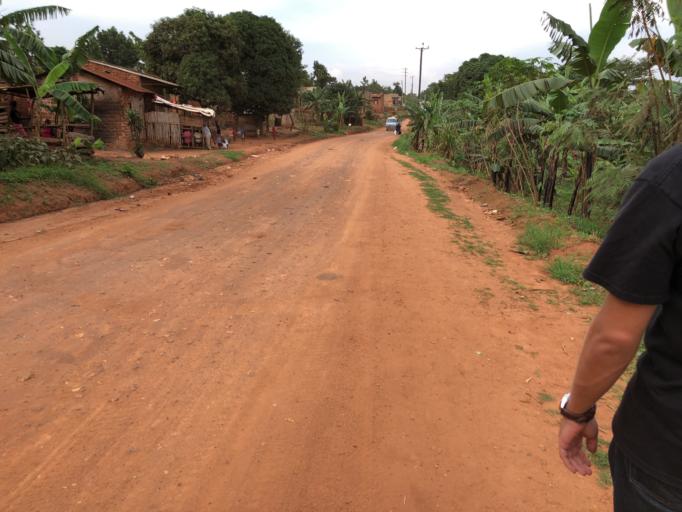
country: UG
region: Central Region
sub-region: Wakiso District
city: Bweyogerere
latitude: 0.4807
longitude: 32.6426
